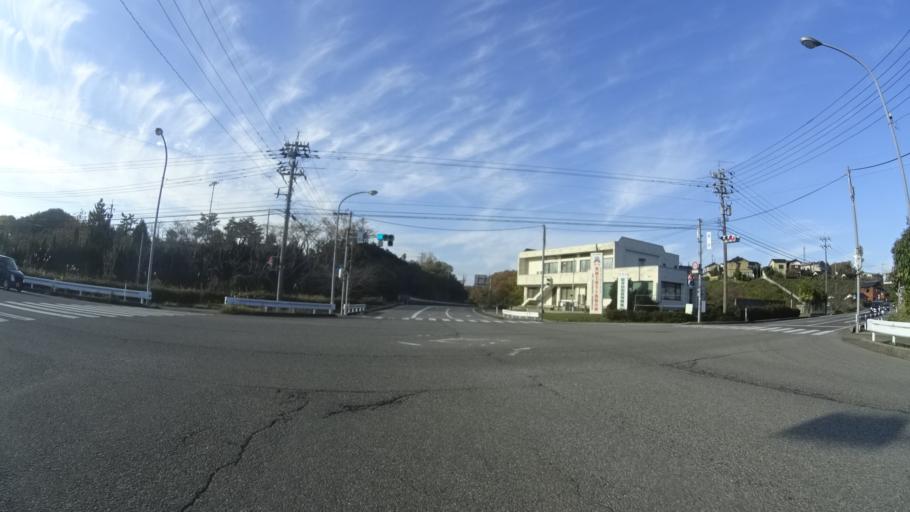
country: JP
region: Ishikawa
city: Hakui
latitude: 37.0225
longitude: 136.7867
